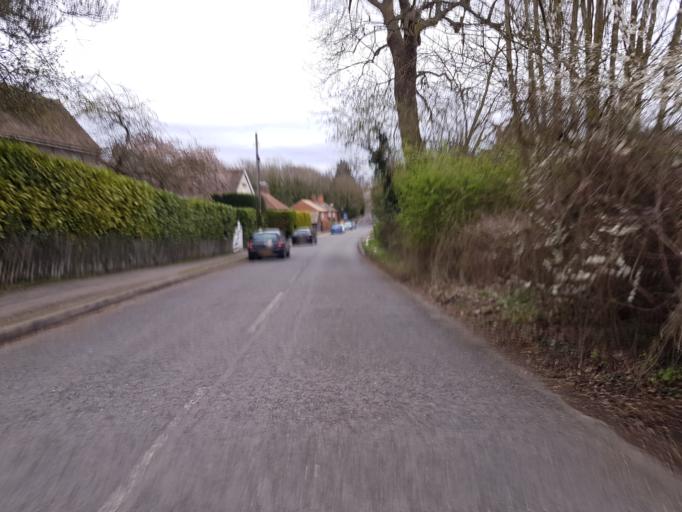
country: GB
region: England
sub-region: Cambridgeshire
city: Girton
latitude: 52.2230
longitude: 0.0445
